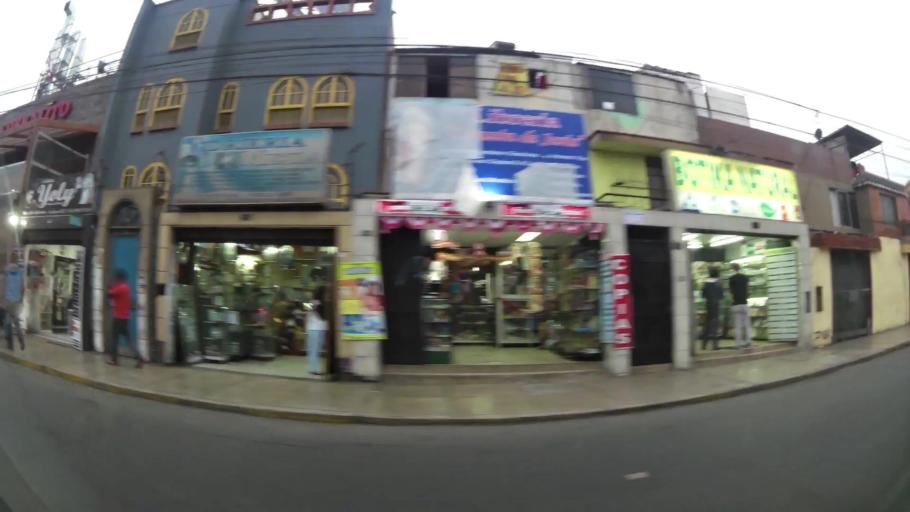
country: PE
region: Lima
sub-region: Lima
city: San Isidro
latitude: -12.0796
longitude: -77.0658
